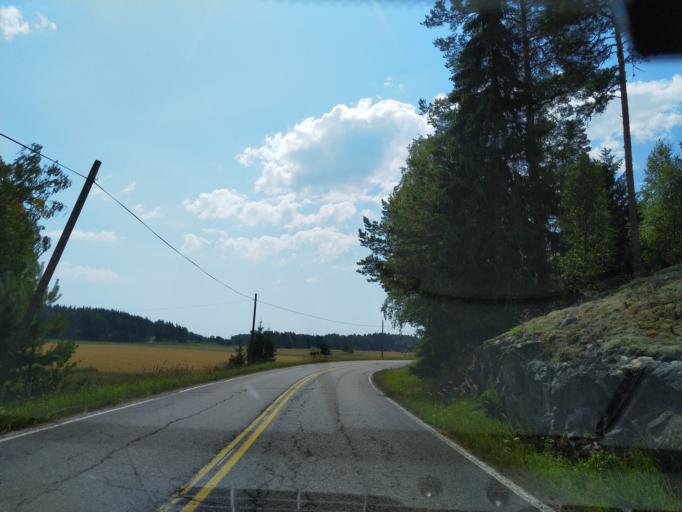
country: FI
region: Uusimaa
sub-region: Helsinki
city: Kirkkonummi
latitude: 60.0186
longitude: 24.4769
